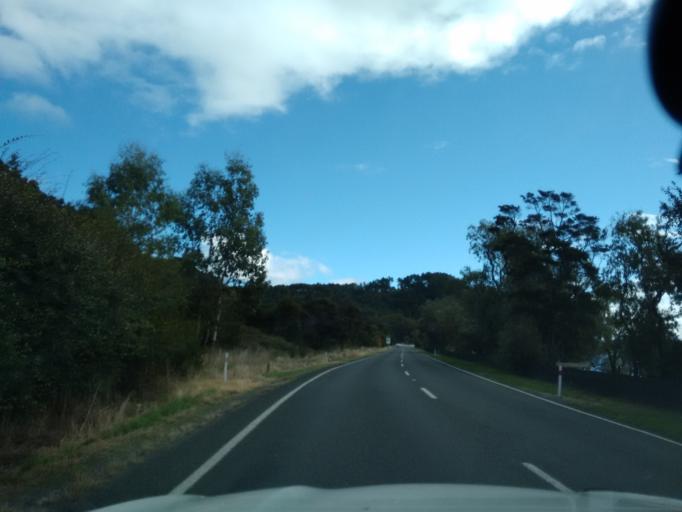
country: NZ
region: Waikato
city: Turangi
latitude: -38.8862
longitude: 175.9633
